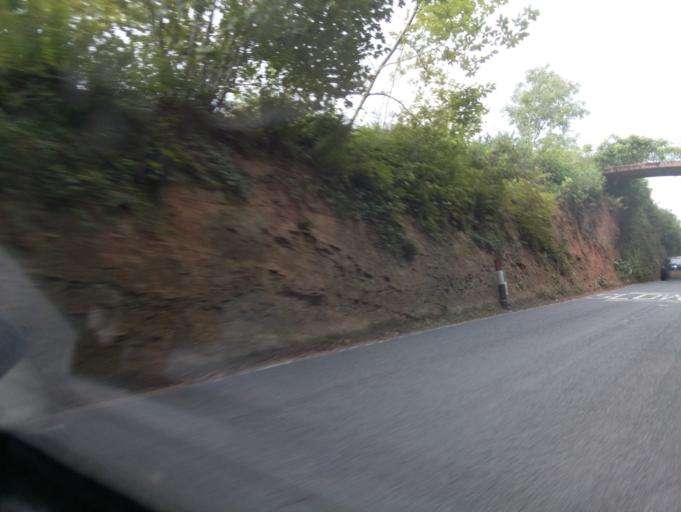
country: GB
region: England
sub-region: Devon
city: Exminster
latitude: 50.6540
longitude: -3.4824
